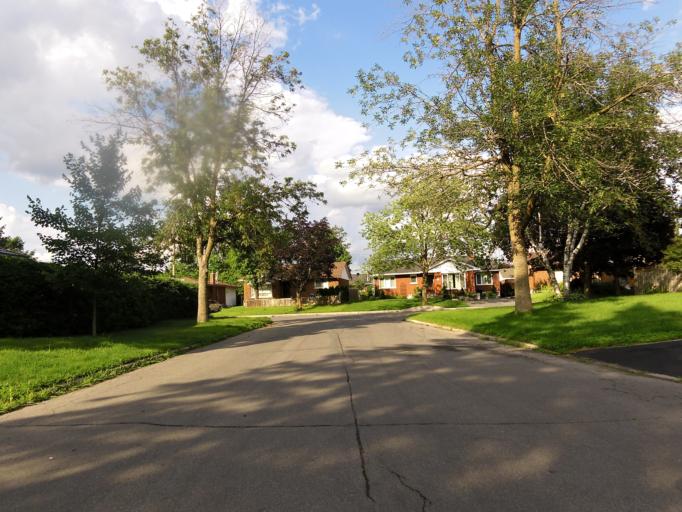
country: CA
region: Ontario
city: Bells Corners
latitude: 45.3485
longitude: -75.7801
